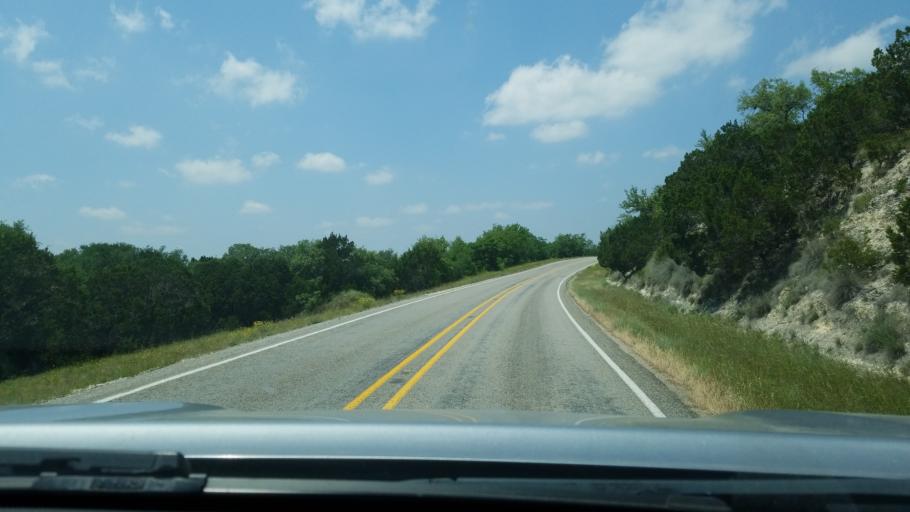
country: US
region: Texas
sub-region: Hays County
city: Woodcreek
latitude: 30.0936
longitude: -98.2339
